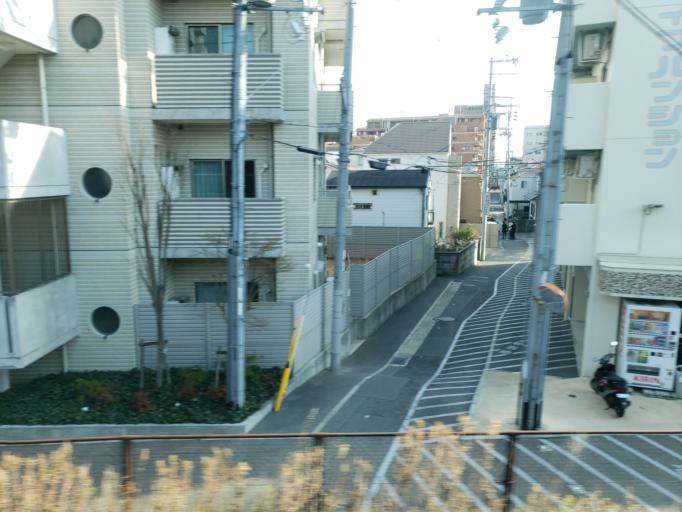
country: JP
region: Hyogo
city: Ashiya
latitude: 34.7229
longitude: 135.2689
